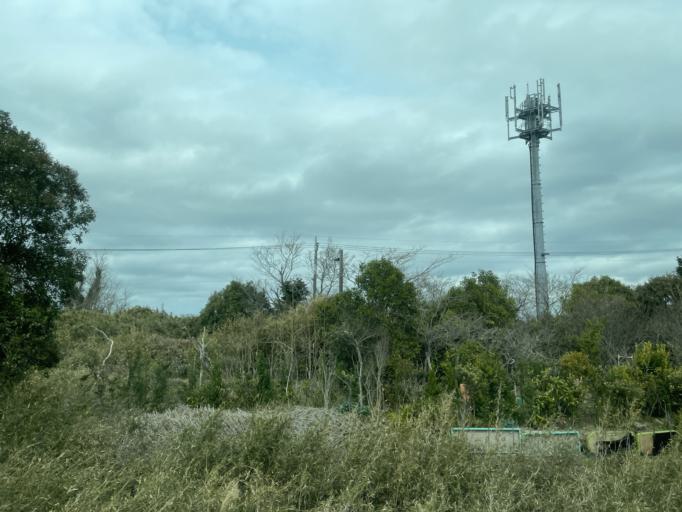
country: JP
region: Ibaraki
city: Ryugasaki
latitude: 35.8395
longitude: 140.2280
